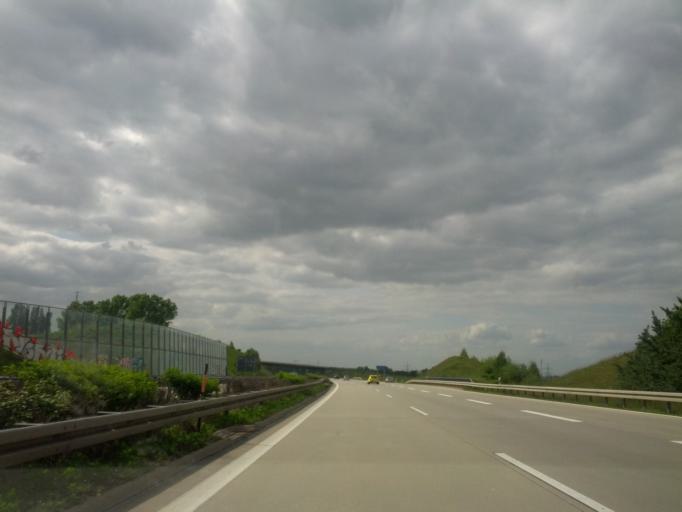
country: DE
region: Saxony
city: Kreischa
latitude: 50.9926
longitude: 13.7682
